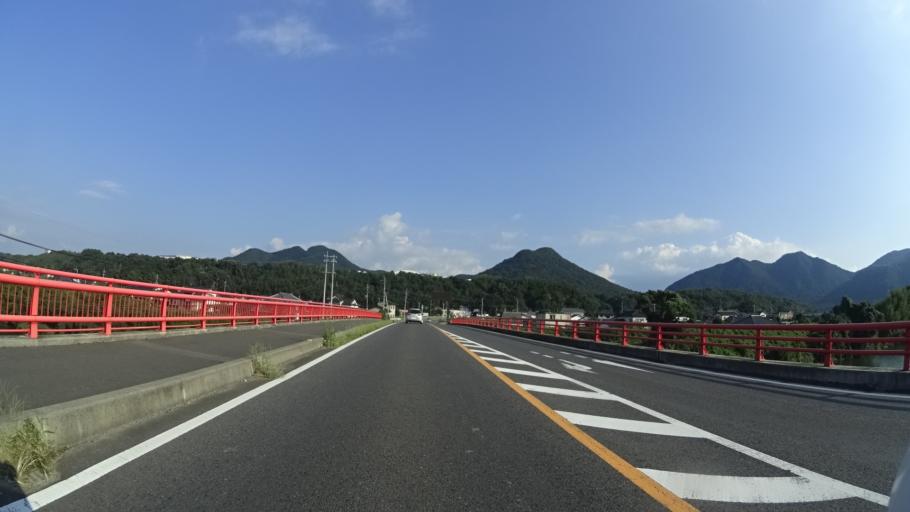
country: JP
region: Oita
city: Bungo-Takada-shi
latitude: 33.5084
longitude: 131.3283
